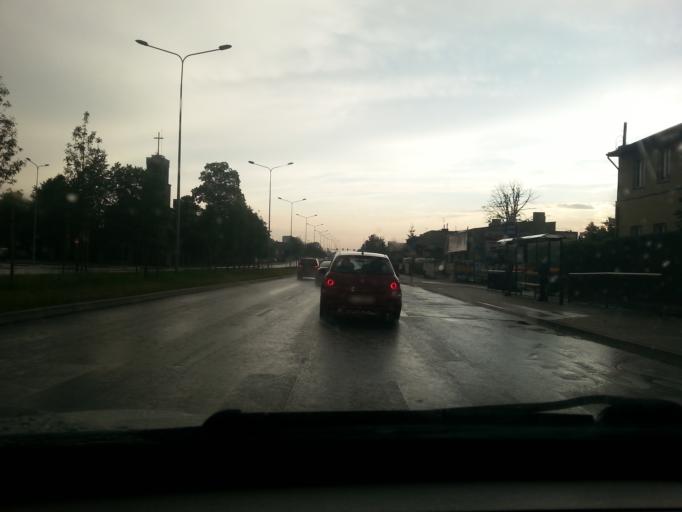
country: PL
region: Lodz Voivodeship
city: Lodz
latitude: 51.8004
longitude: 19.4774
